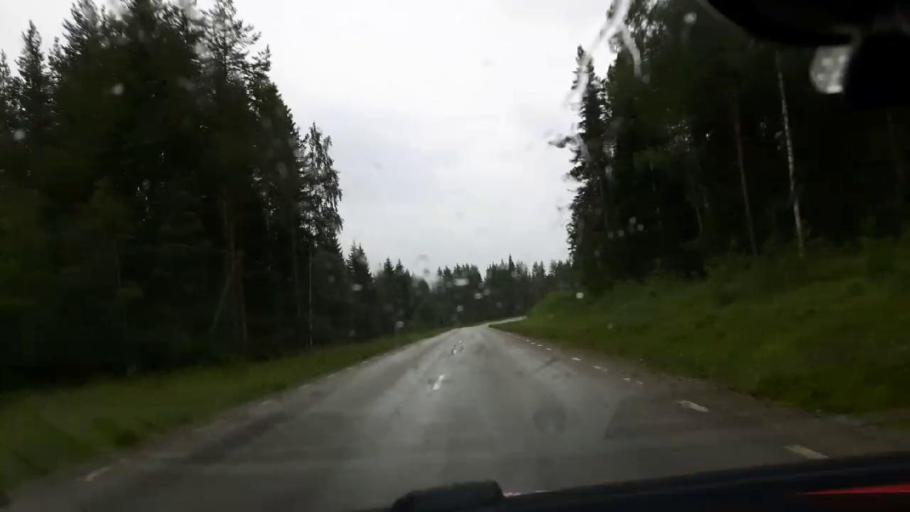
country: SE
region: Jaemtland
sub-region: OEstersunds Kommun
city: Brunflo
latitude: 62.8329
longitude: 15.0075
